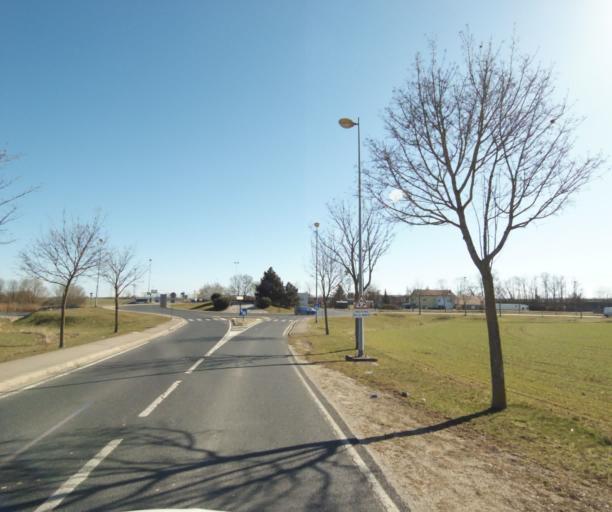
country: FR
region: Lorraine
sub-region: Departement de Meurthe-et-Moselle
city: Fleville-devant-Nancy
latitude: 48.6200
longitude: 6.2028
